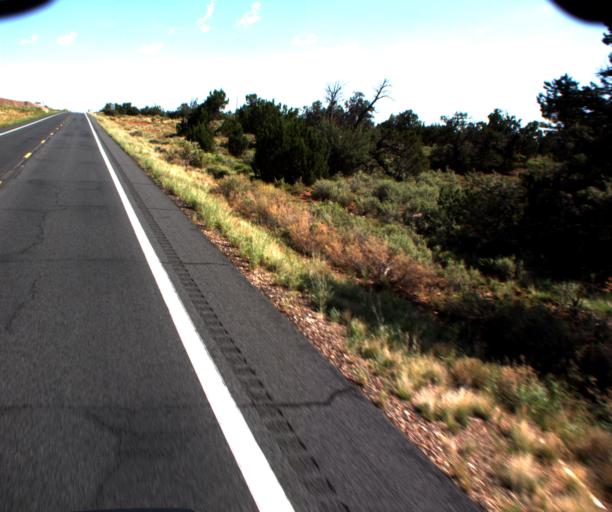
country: US
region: Arizona
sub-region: Coconino County
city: Williams
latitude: 35.6410
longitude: -112.1410
